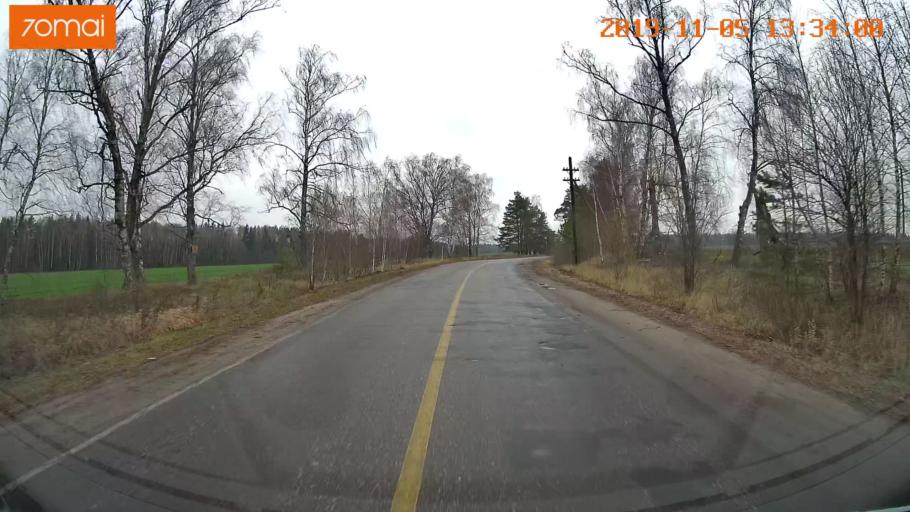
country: RU
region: Ivanovo
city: Shuya
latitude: 56.8970
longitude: 41.3904
